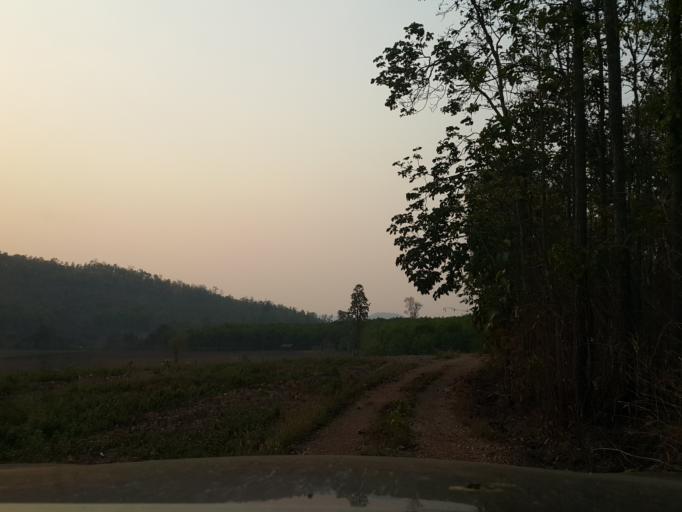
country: TH
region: Lamphun
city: Thung Hua Chang
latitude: 17.9154
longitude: 99.0734
